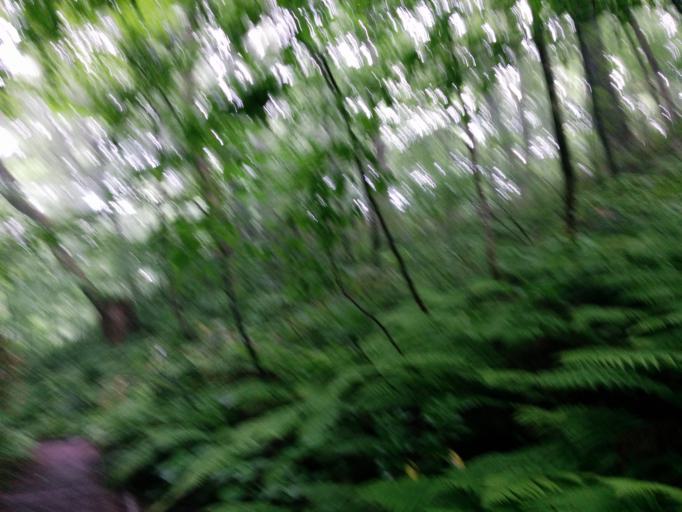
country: JP
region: Akita
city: Noshiromachi
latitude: 40.5630
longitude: 139.9795
